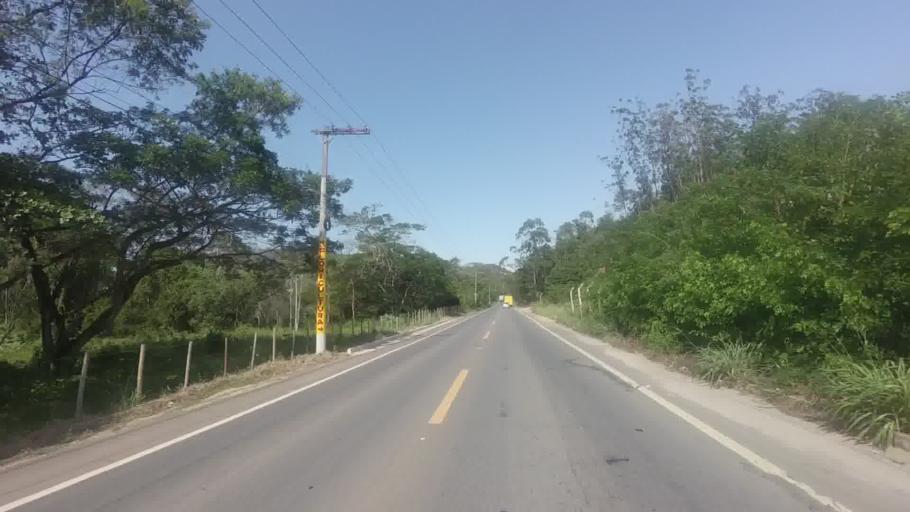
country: BR
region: Espirito Santo
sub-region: Piuma
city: Piuma
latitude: -20.8186
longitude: -40.6916
